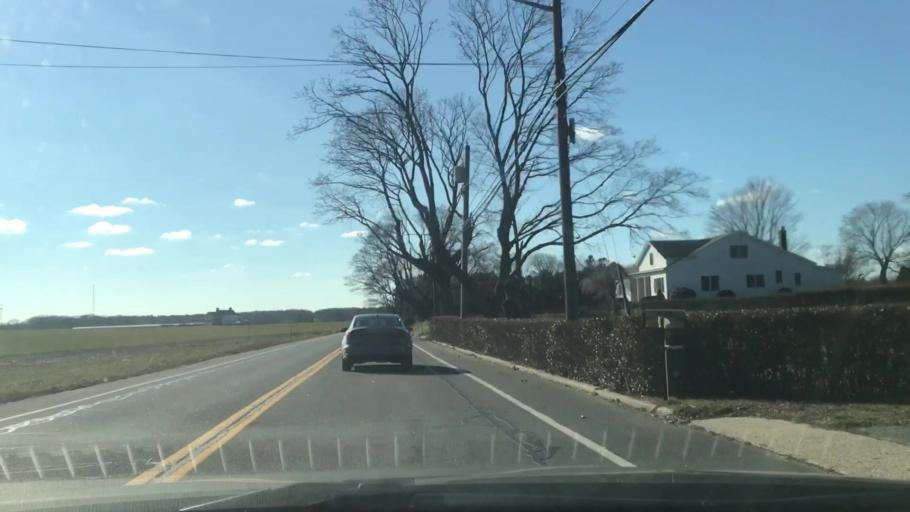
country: US
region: New York
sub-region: Suffolk County
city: Aquebogue
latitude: 40.9527
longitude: -72.6539
